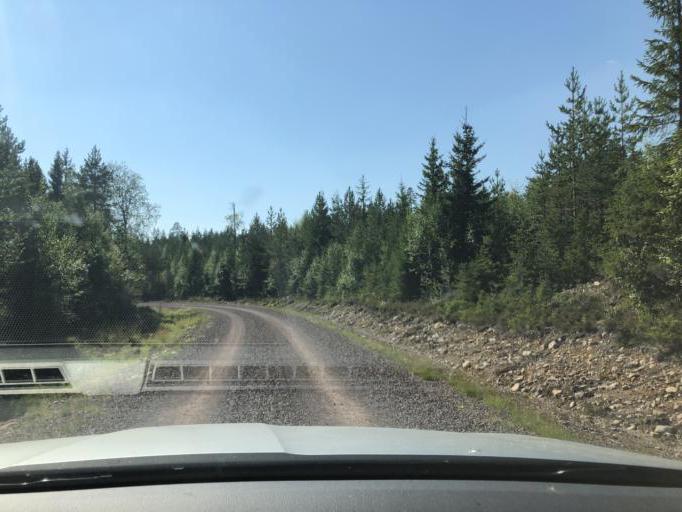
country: SE
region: Dalarna
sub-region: Orsa Kommun
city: Orsa
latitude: 61.2554
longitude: 14.7318
